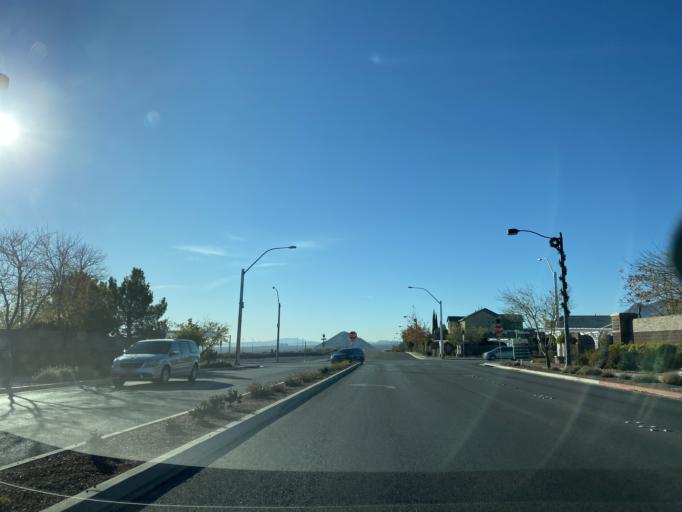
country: US
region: Nevada
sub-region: Clark County
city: Summerlin South
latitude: 36.2890
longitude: -115.3196
